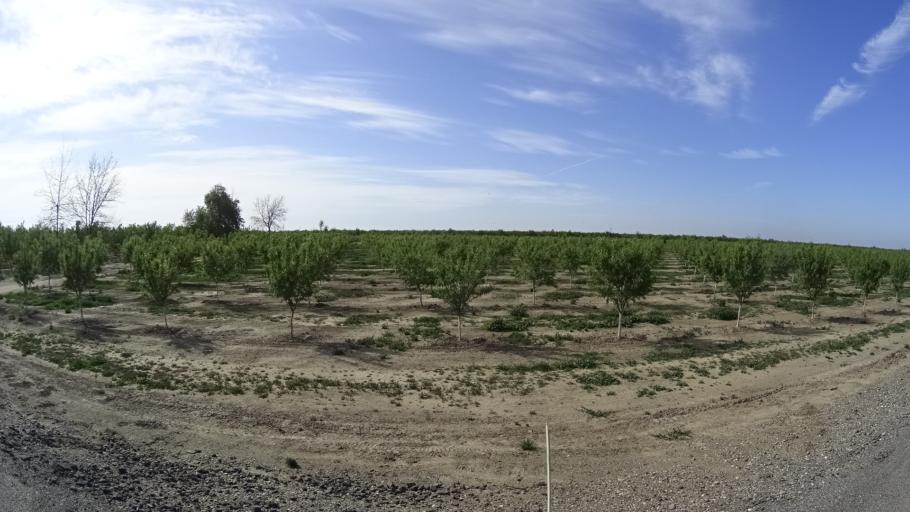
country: US
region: California
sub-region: Glenn County
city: Hamilton City
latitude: 39.6233
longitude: -122.0094
